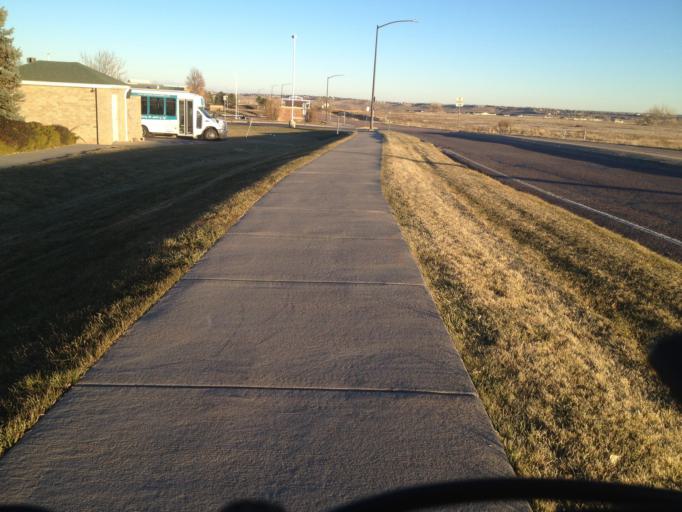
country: US
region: Colorado
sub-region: Boulder County
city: Superior
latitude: 39.9510
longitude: -105.1459
